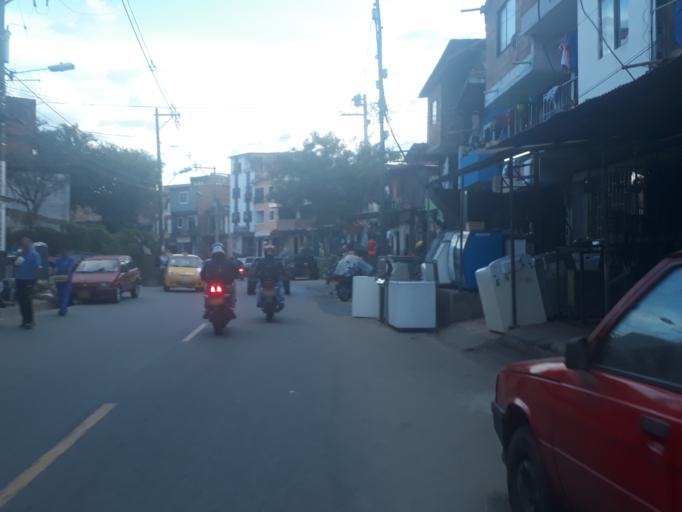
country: CO
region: Antioquia
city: Medellin
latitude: 6.2828
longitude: -75.5659
